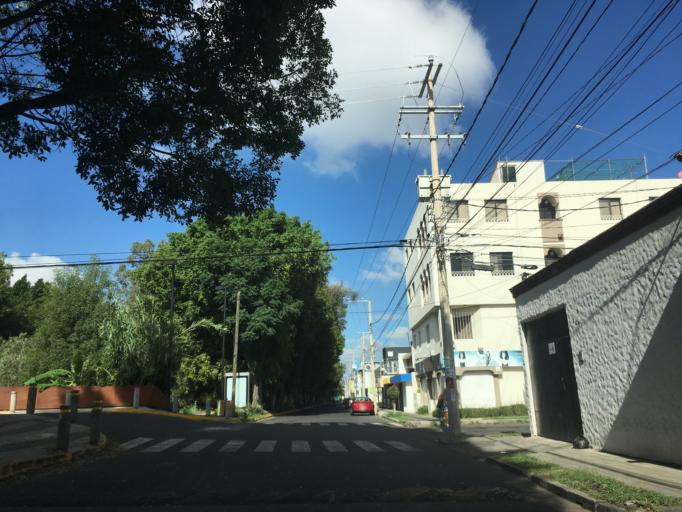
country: MX
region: Michoacan
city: Morelia
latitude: 19.6870
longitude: -101.1755
